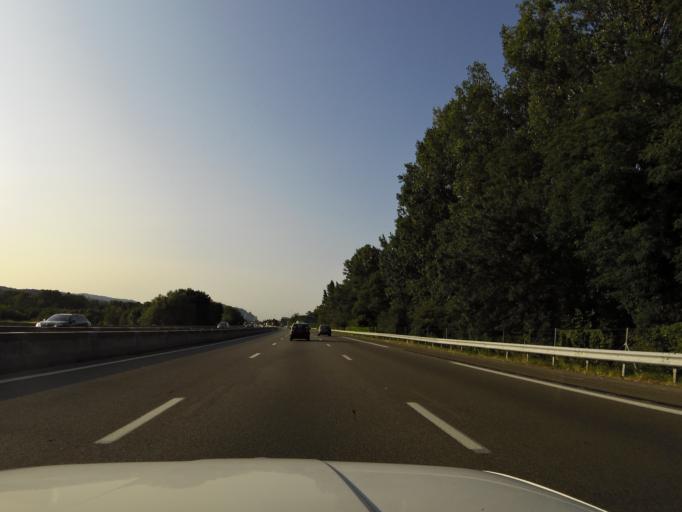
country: FR
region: Rhone-Alpes
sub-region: Departement de la Drome
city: Portes-les-Valence
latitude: 44.8586
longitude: 4.8669
